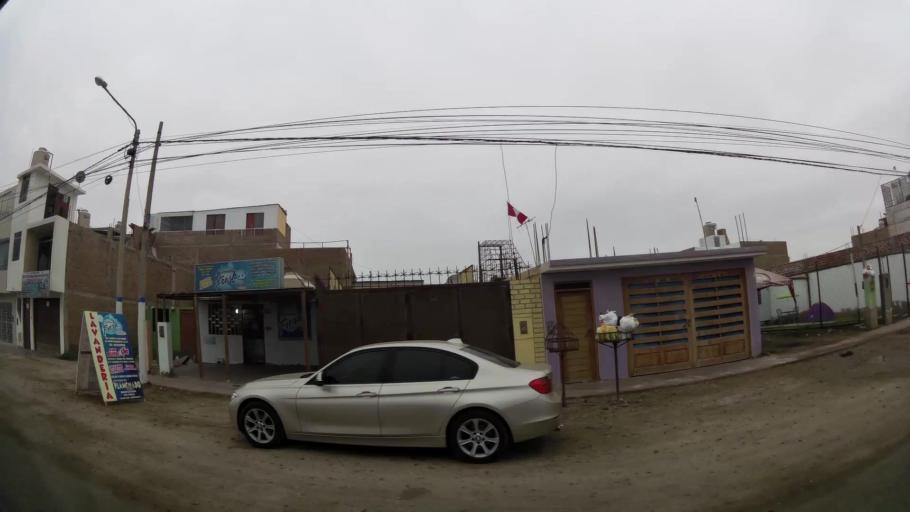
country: PE
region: Ica
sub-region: Provincia de Pisco
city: Pisco
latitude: -13.7196
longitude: -76.2205
